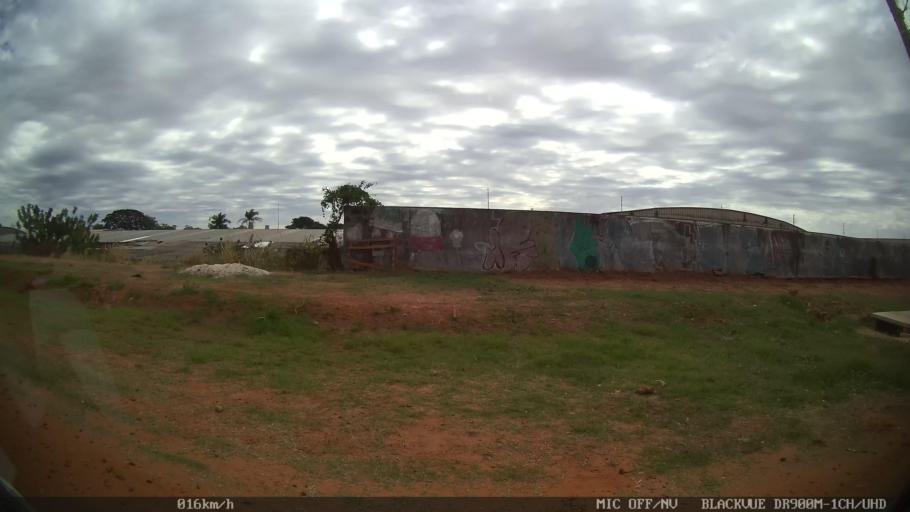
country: BR
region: Sao Paulo
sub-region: Bady Bassitt
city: Bady Bassitt
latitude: -20.8108
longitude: -49.5001
